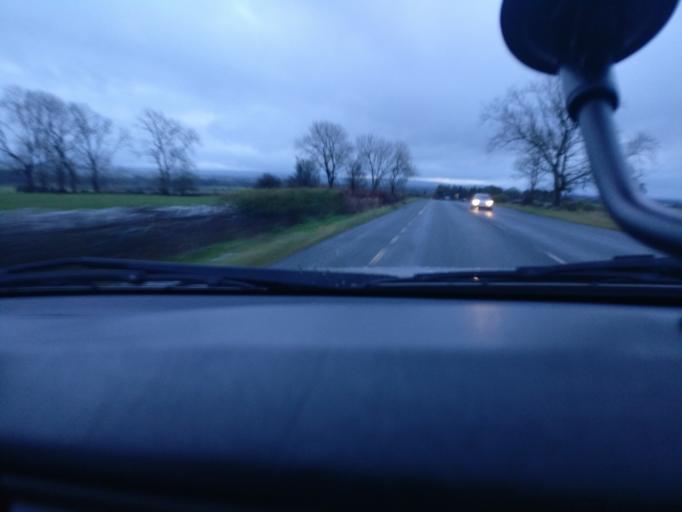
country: IE
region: Connaught
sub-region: County Galway
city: Loughrea
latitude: 53.2632
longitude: -8.4217
